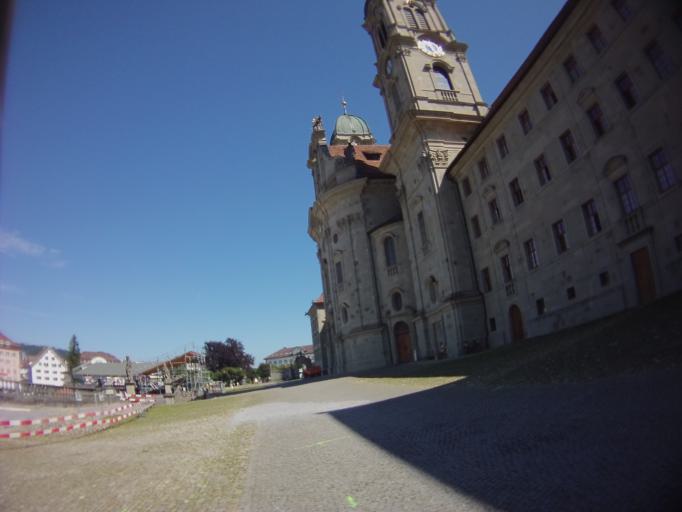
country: CH
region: Schwyz
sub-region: Bezirk Einsiedeln
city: Einsiedeln
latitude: 47.1261
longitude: 8.7515
